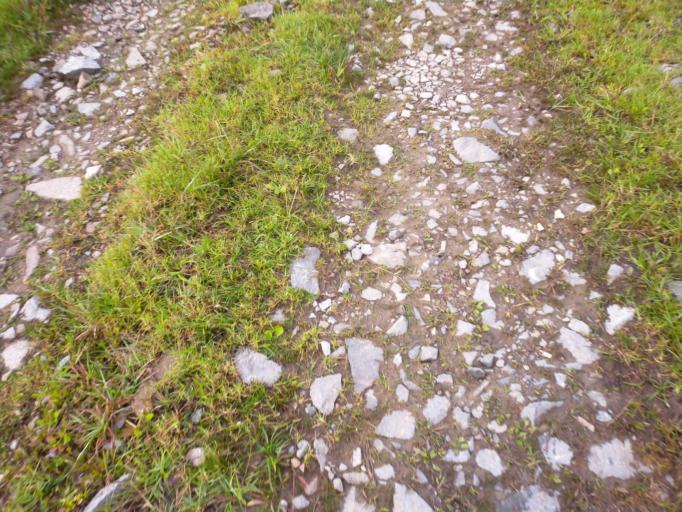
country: PG
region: Enga
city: Porgera
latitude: -5.4607
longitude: 143.1057
